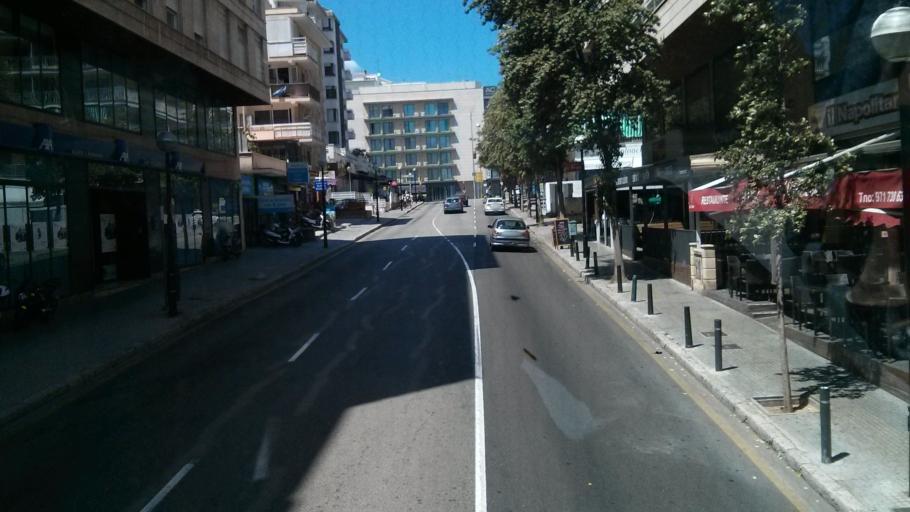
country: ES
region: Balearic Islands
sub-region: Illes Balears
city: Palma
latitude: 39.5693
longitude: 2.6345
